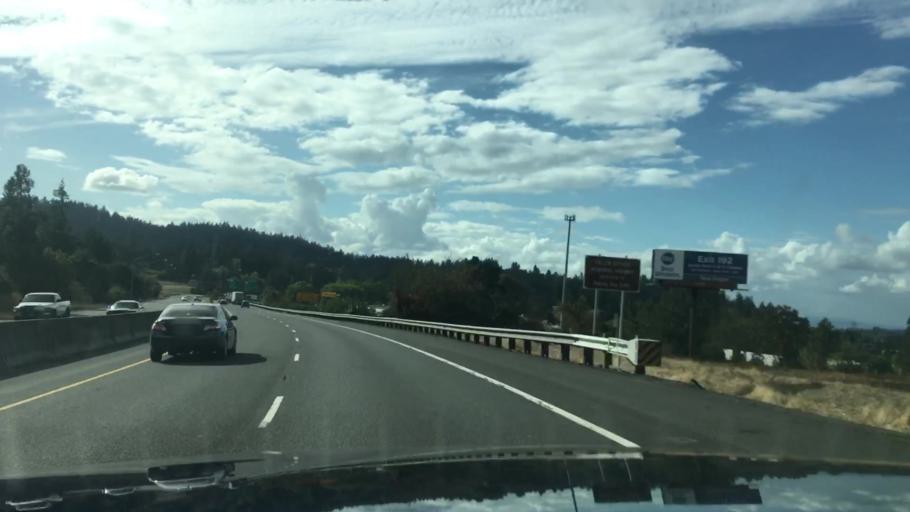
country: US
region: Oregon
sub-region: Lane County
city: Springfield
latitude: 44.0352
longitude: -123.0348
